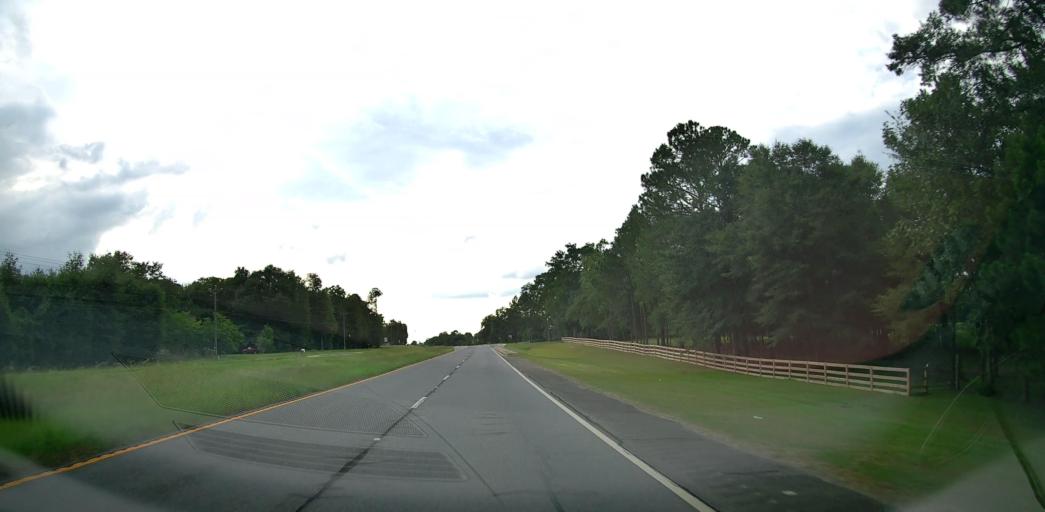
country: US
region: Georgia
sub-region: Pulaski County
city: Hawkinsville
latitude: 32.2766
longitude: -83.4247
